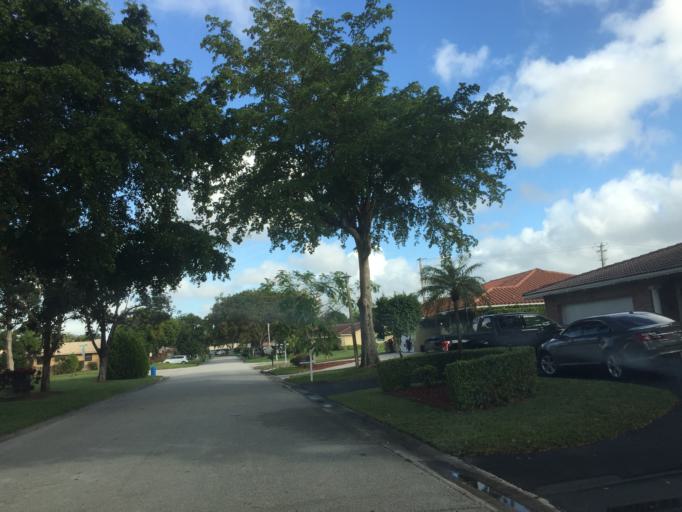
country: US
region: Florida
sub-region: Broward County
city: North Lauderdale
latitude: 26.2418
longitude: -80.2347
